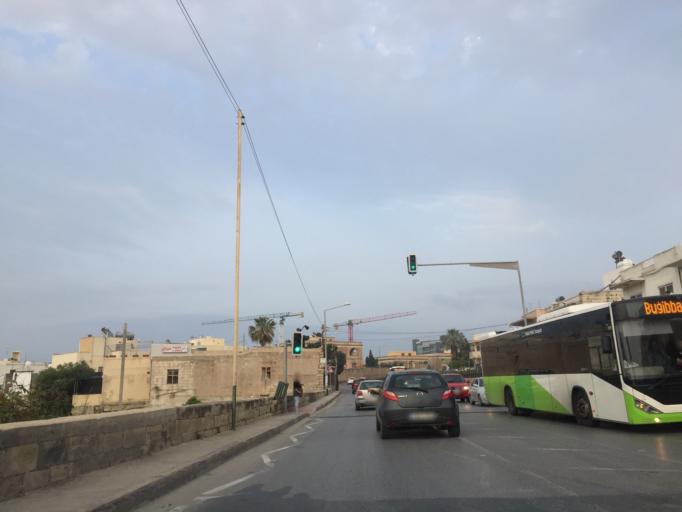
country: MT
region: Is-Swieqi
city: Swieqi
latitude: 35.9236
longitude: 14.4833
